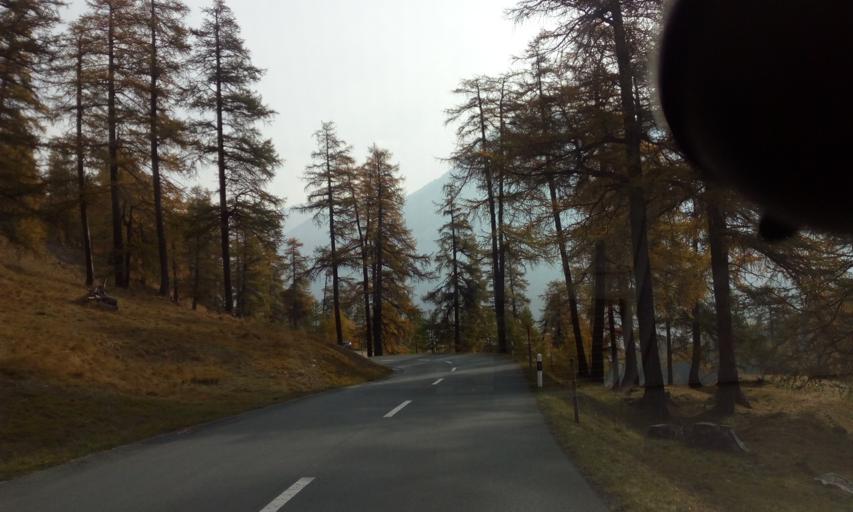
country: CH
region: Grisons
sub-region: Maloja District
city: Ponte
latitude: 46.5826
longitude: 9.9086
